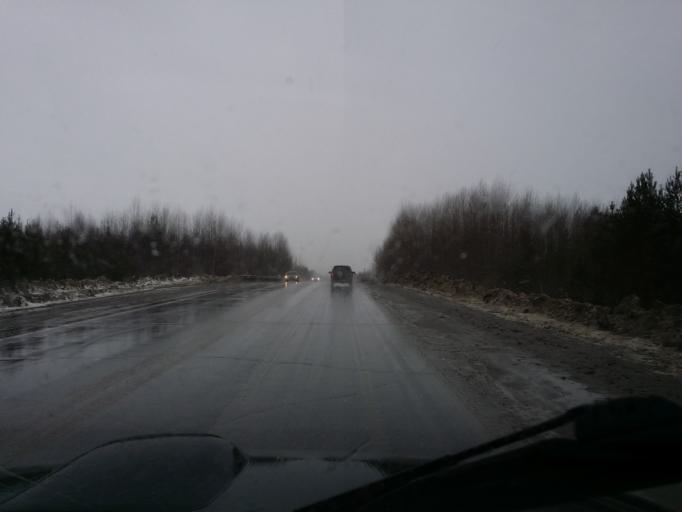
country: RU
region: Khanty-Mansiyskiy Avtonomnyy Okrug
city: Izluchinsk
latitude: 60.9653
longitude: 76.8097
